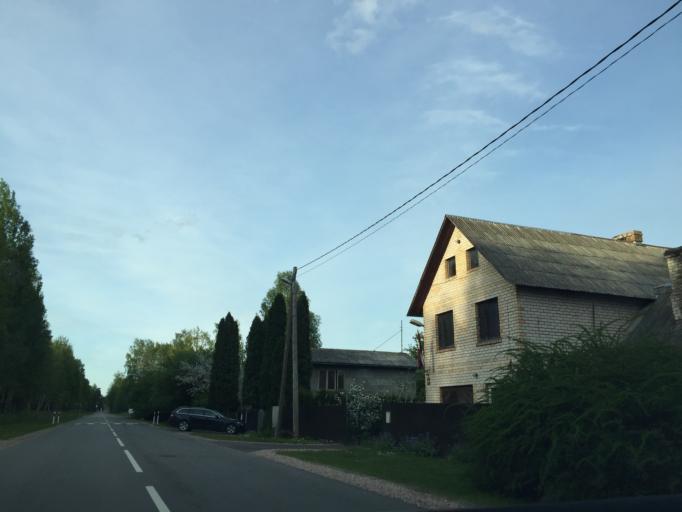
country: LV
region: Ozolnieku
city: Ozolnieki
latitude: 56.6557
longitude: 23.7786
